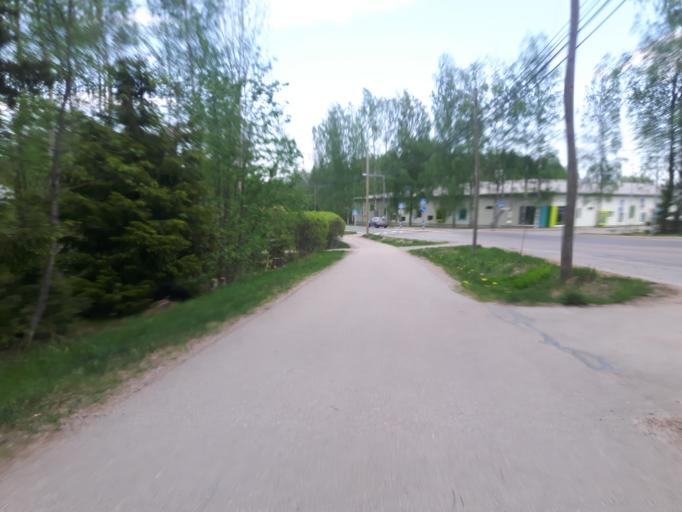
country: FI
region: Uusimaa
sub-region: Porvoo
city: Porvoo
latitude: 60.4012
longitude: 25.7034
